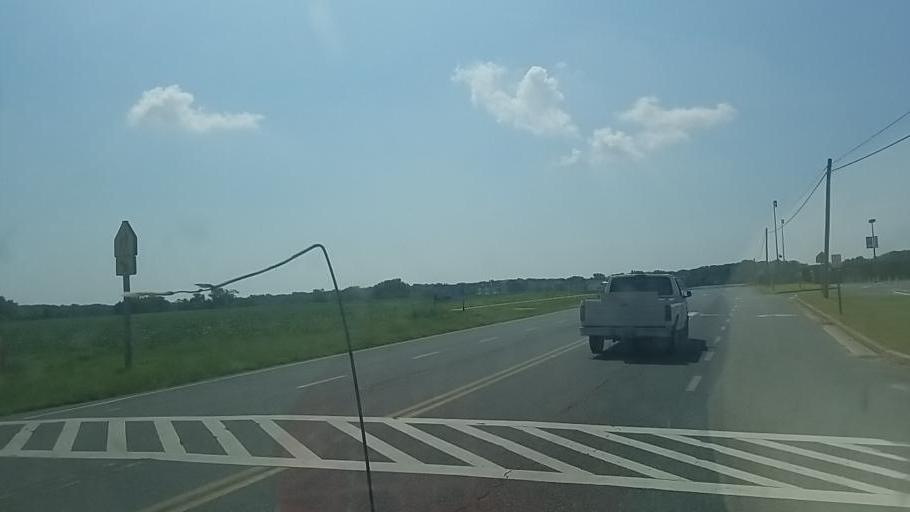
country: US
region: Maryland
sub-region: Worcester County
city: Berlin
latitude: 38.3418
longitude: -75.1892
